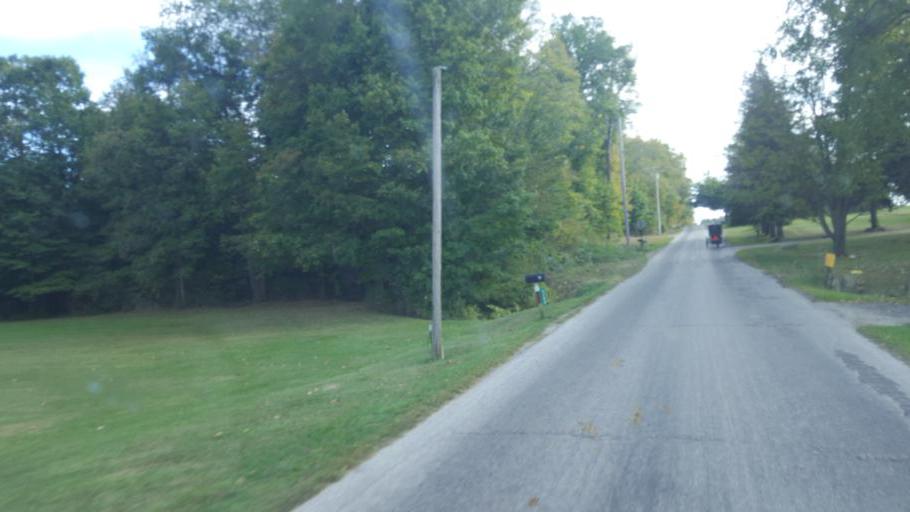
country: US
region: Ohio
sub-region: Richland County
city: Lexington
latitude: 40.5857
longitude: -82.6051
